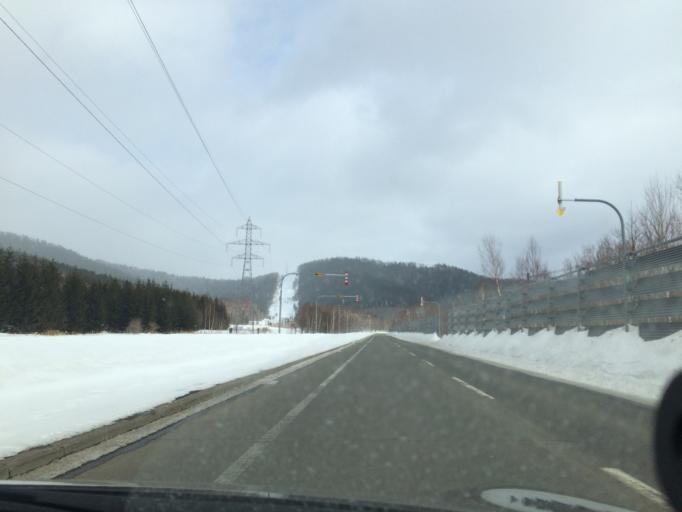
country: JP
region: Hokkaido
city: Shimo-furano
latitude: 43.0545
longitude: 142.6361
